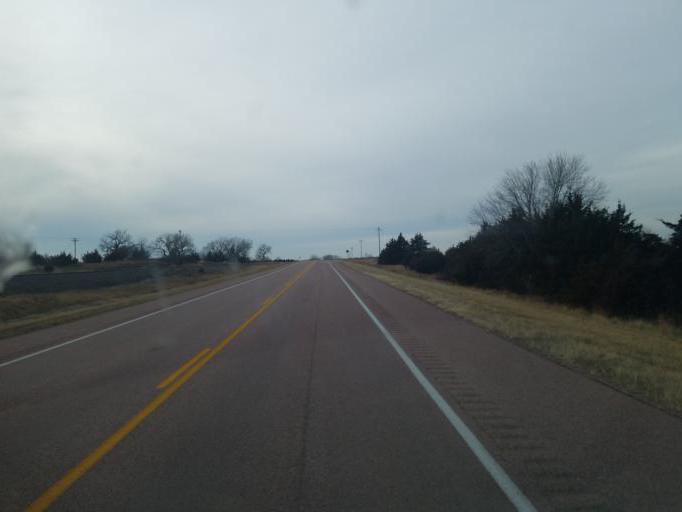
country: US
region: Nebraska
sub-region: Antelope County
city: Neligh
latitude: 42.3363
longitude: -98.0757
